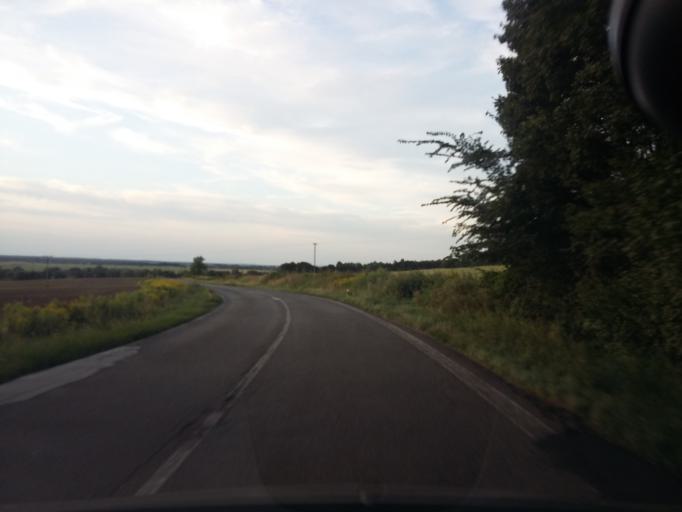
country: SK
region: Bratislavsky
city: Svaty Jur
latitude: 48.3738
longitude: 17.1491
